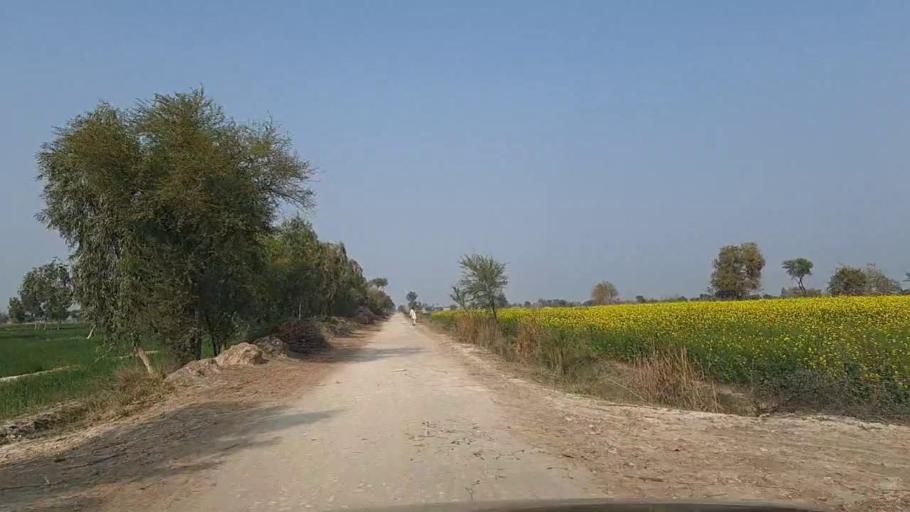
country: PK
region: Sindh
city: Daur
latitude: 26.4005
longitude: 68.4239
